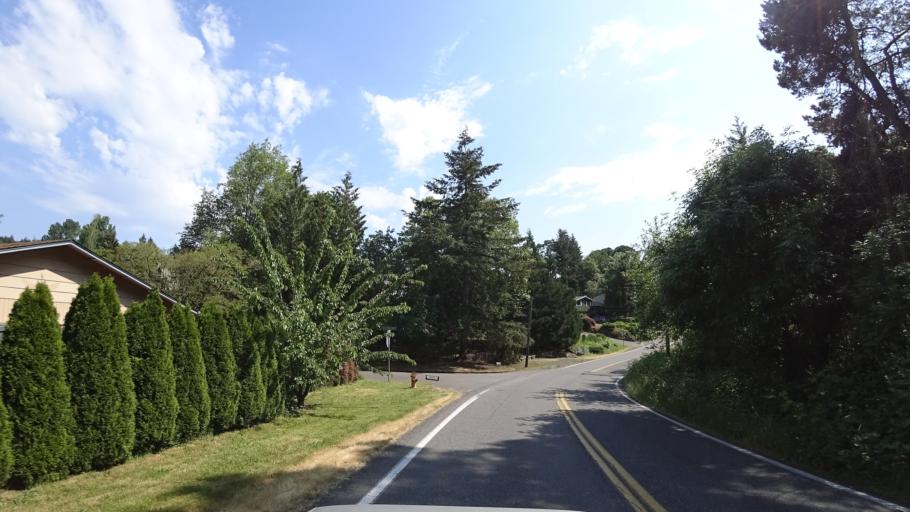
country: US
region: Oregon
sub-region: Washington County
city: Metzger
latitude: 45.4492
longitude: -122.7382
